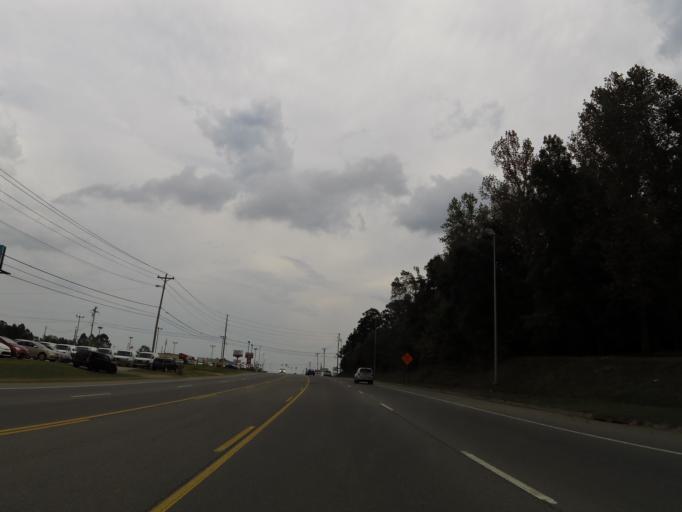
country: US
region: Tennessee
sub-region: Dickson County
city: Burns
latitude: 36.0346
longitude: -87.3546
